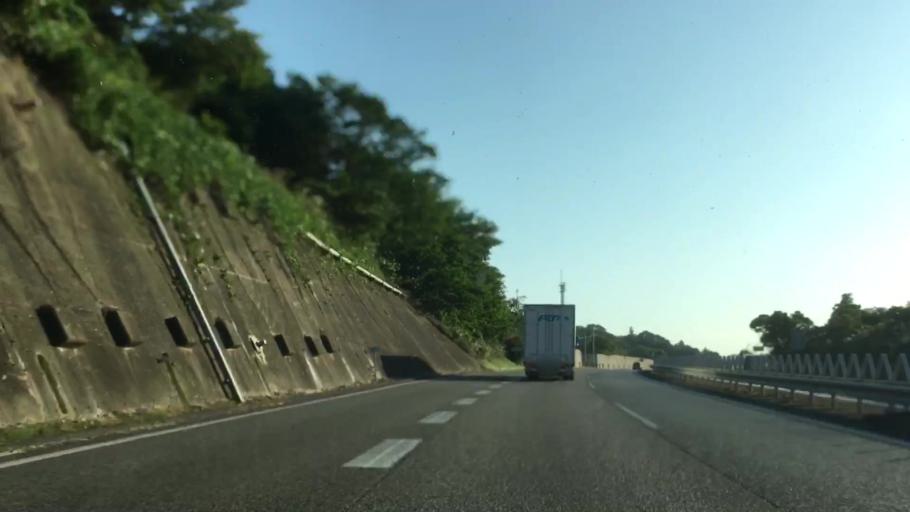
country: JP
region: Yamaguchi
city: Onoda
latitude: 34.1477
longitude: 131.2337
